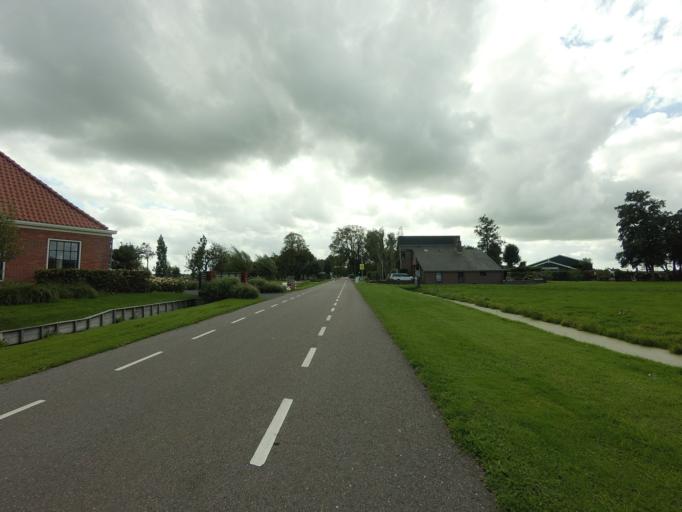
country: NL
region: North Holland
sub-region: Gemeente Edam-Volendam
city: Edam
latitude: 52.5376
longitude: 5.0146
